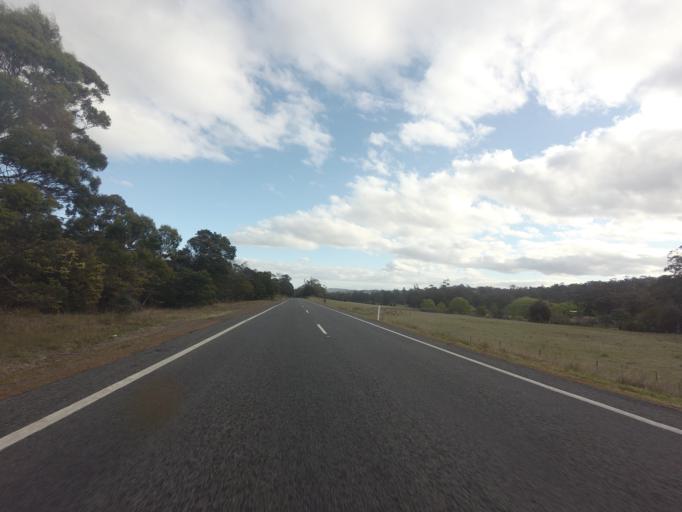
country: AU
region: Tasmania
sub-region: Sorell
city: Sorell
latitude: -42.6888
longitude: 147.5283
